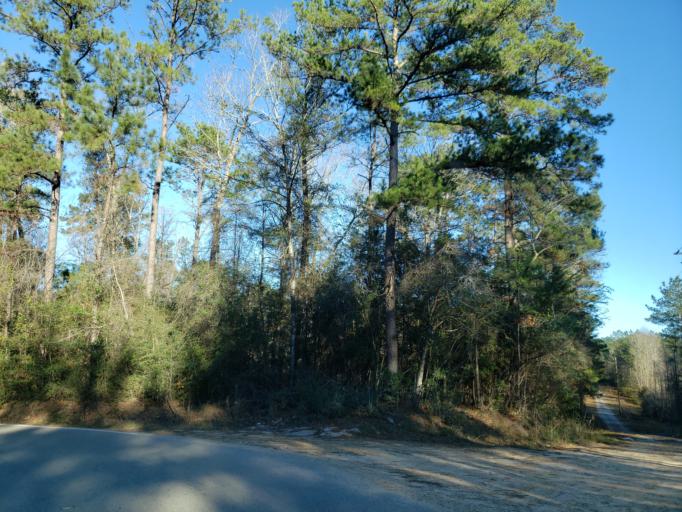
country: US
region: Mississippi
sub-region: Lamar County
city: Arnold Line
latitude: 31.3467
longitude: -89.3777
